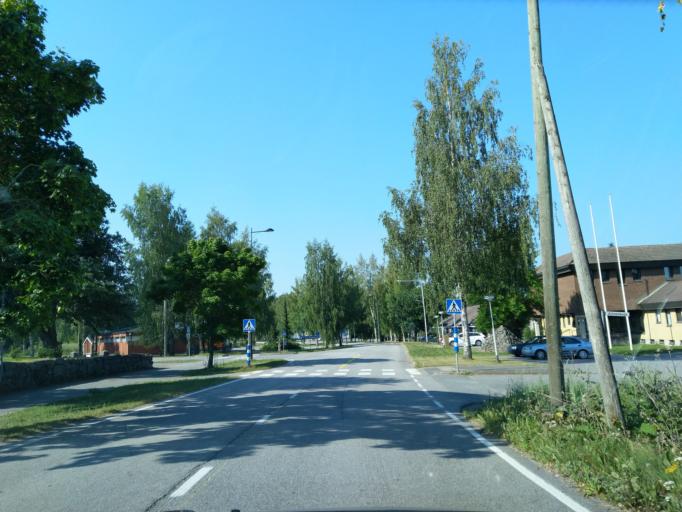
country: FI
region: Satakunta
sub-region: Pori
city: Pomarkku
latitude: 61.6938
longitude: 22.0094
